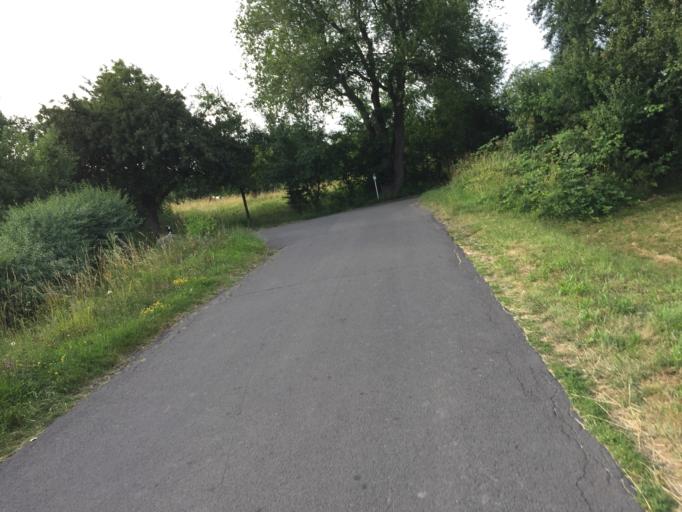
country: DE
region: Hesse
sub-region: Regierungsbezirk Giessen
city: Reiskirchen
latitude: 50.6000
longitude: 8.8338
